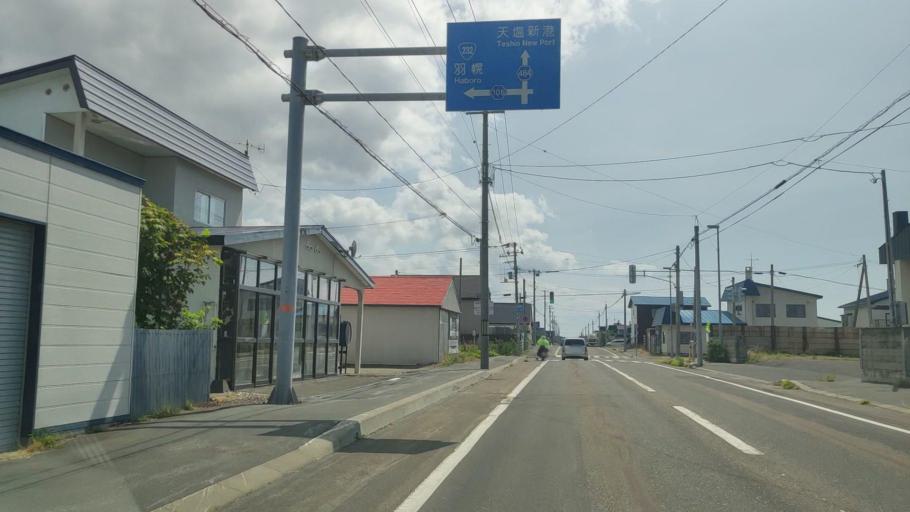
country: JP
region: Hokkaido
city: Makubetsu
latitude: 44.8833
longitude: 141.7429
